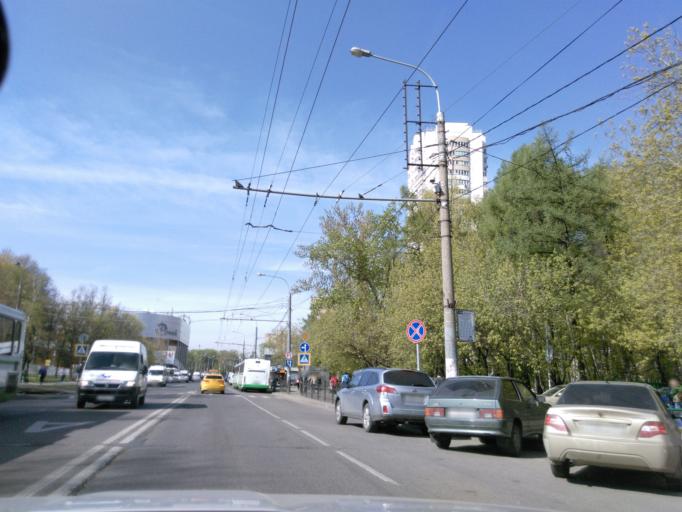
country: RU
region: Moskovskaya
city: Levoberezhnyy
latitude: 55.8567
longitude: 37.4808
